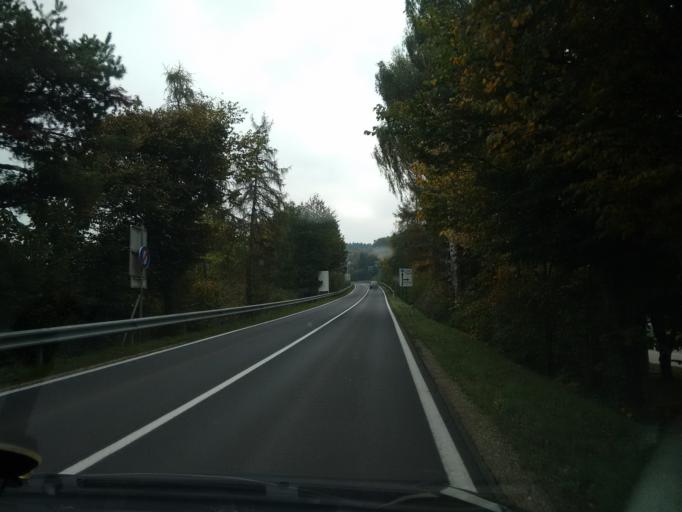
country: AT
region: Upper Austria
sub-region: Politischer Bezirk Kirchdorf an der Krems
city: Kremsmunster
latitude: 48.0503
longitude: 14.1286
